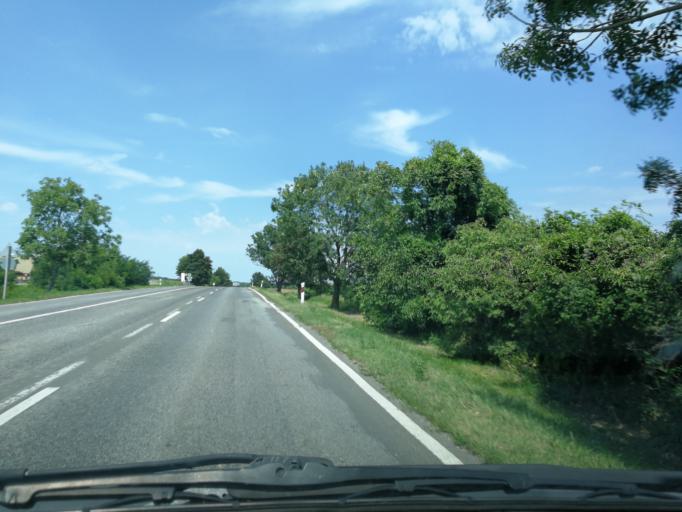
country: HU
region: Baranya
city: Pecsvarad
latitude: 46.1709
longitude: 18.4380
